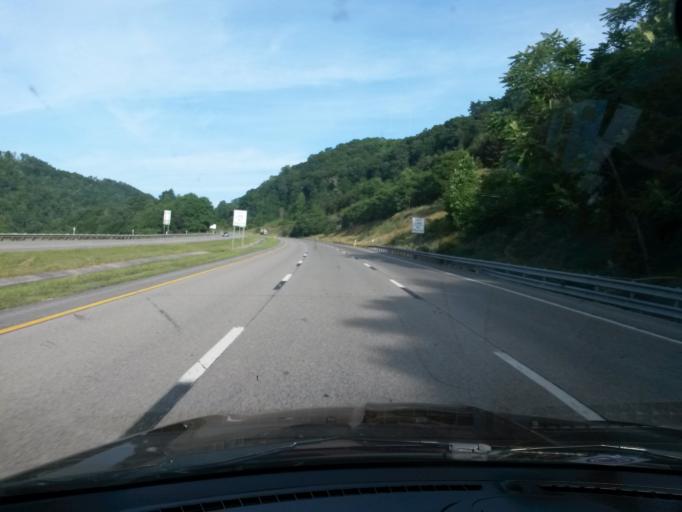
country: US
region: West Virginia
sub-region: Summers County
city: Hinton
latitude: 37.7820
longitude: -80.9433
